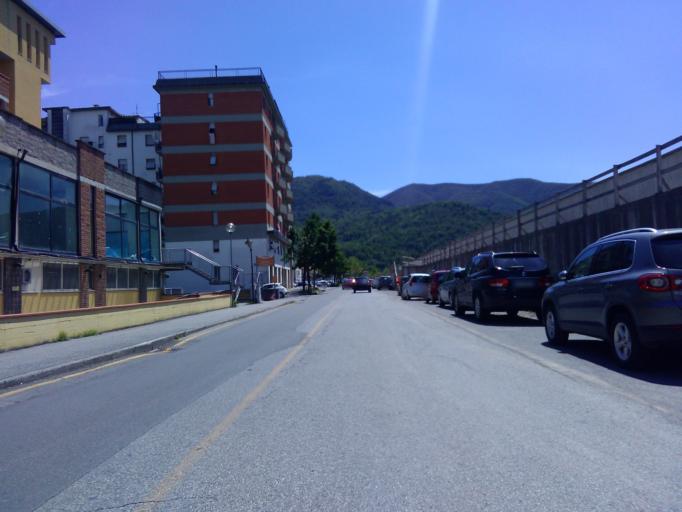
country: IT
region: Tuscany
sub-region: Provincia di Massa-Carrara
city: Aulla
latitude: 44.2106
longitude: 9.9672
